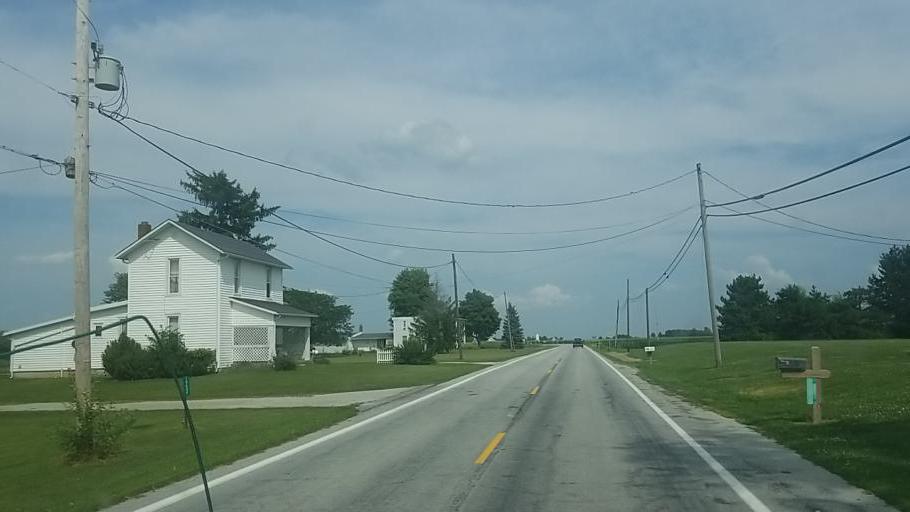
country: US
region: Ohio
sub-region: Hardin County
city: Forest
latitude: 40.8018
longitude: -83.5012
